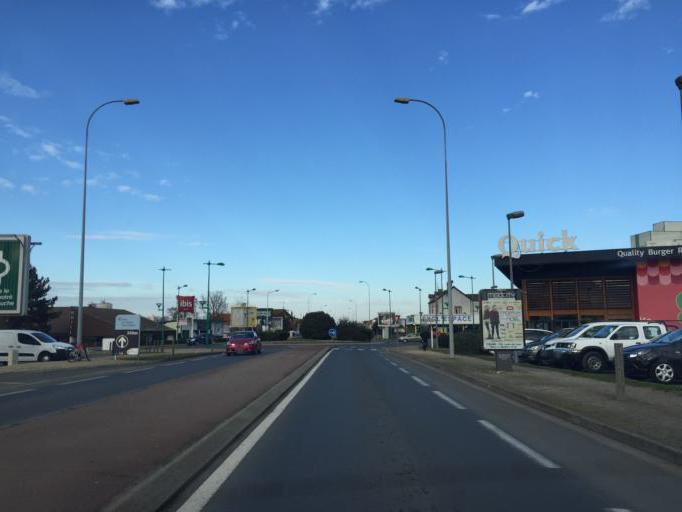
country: FR
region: Auvergne
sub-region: Departement de l'Allier
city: Yzeure
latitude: 46.5423
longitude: 3.3436
